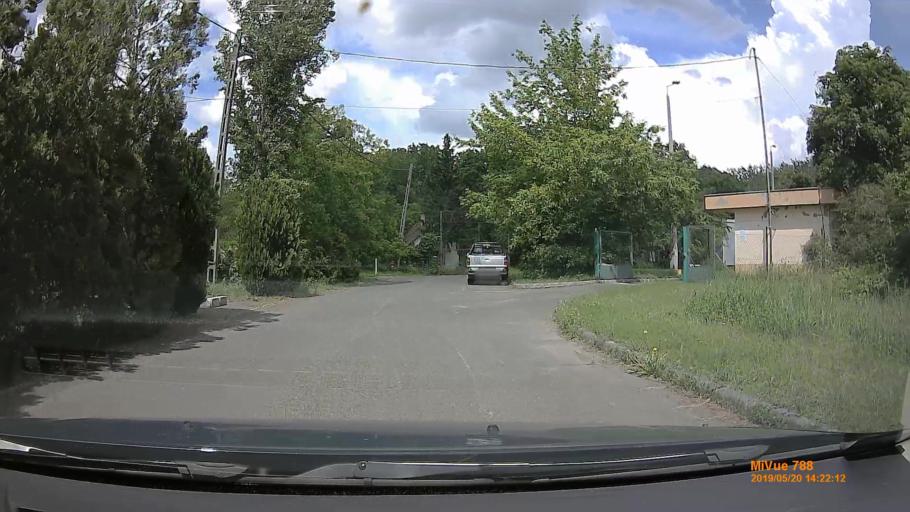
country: HU
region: Budapest
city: Budapest XVII. keruelet
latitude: 47.4860
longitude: 19.2300
